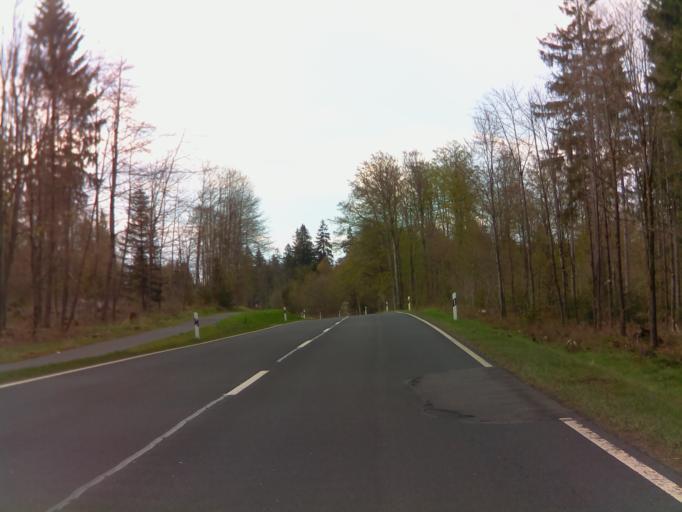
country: DE
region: Bavaria
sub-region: Upper Franconia
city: Ludwigsstadt
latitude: 50.4547
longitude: 11.3492
